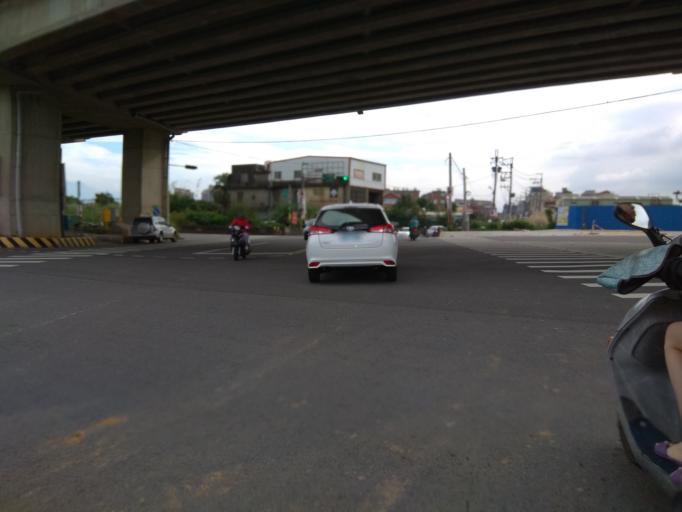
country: TW
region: Taiwan
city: Daxi
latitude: 24.9288
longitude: 121.2058
